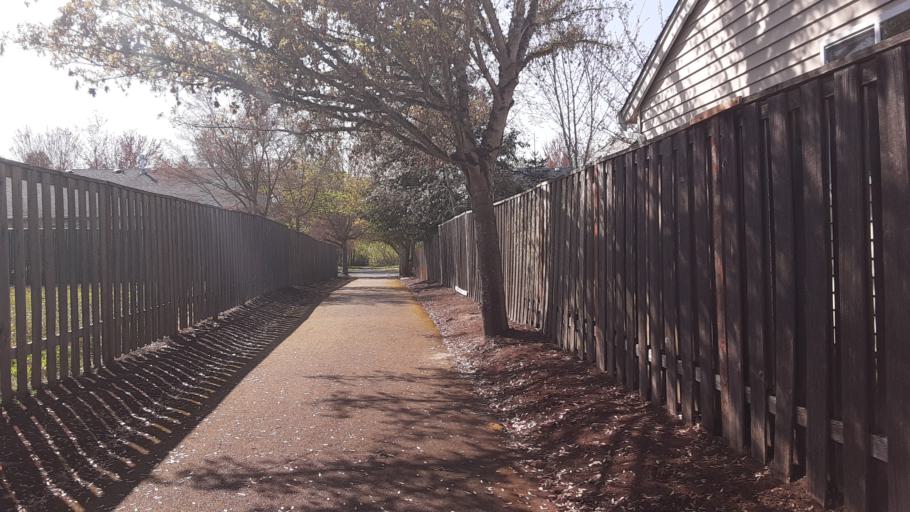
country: US
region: Oregon
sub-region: Benton County
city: Corvallis
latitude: 44.5344
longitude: -123.2558
